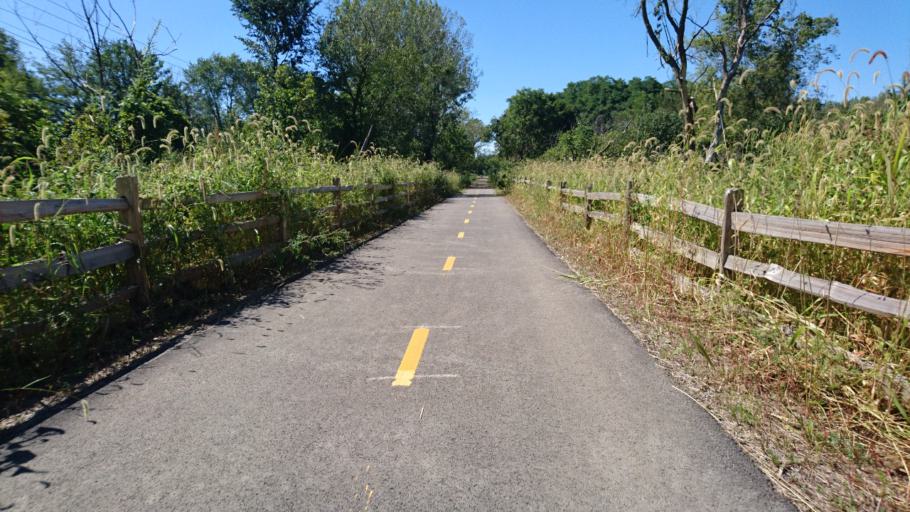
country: US
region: Illinois
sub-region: Cook County
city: Park Forest
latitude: 41.4991
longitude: -87.6704
